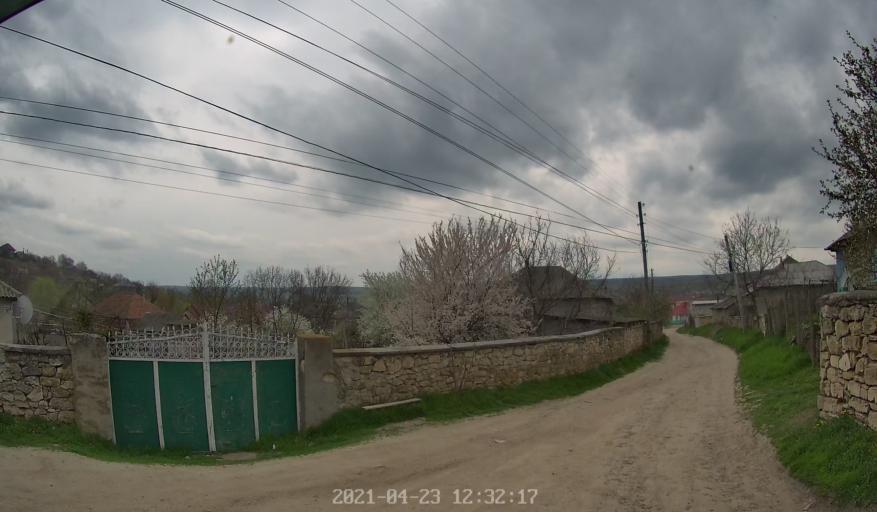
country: MD
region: Chisinau
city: Vadul lui Voda
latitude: 47.1278
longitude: 28.9998
